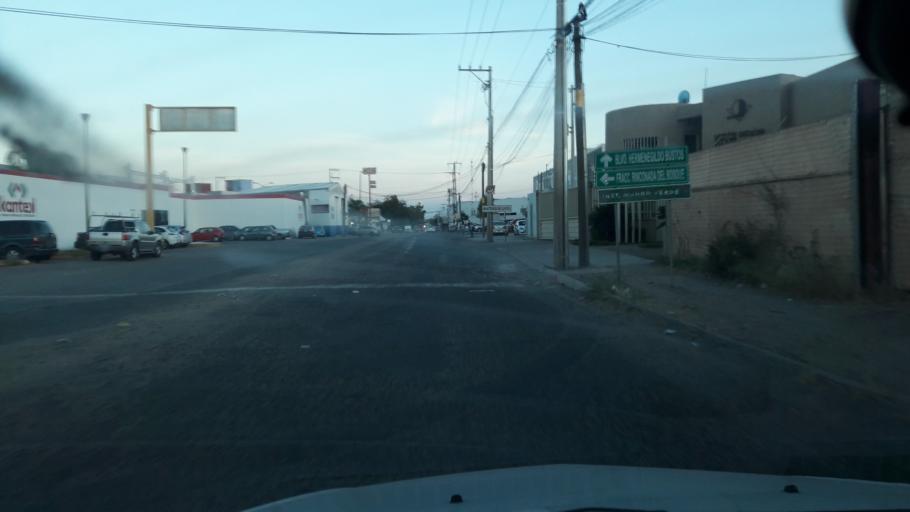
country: MX
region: Guanajuato
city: Leon
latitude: 21.1701
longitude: -101.6793
